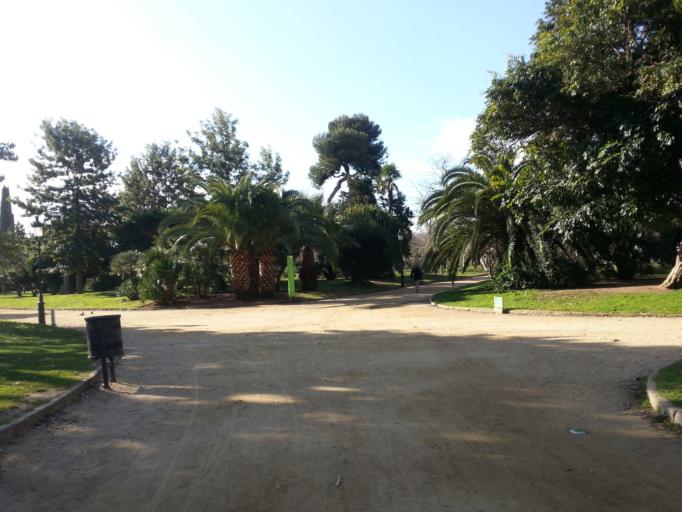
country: ES
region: Catalonia
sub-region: Provincia de Barcelona
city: Ciutat Vella
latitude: 41.3886
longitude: 2.1860
